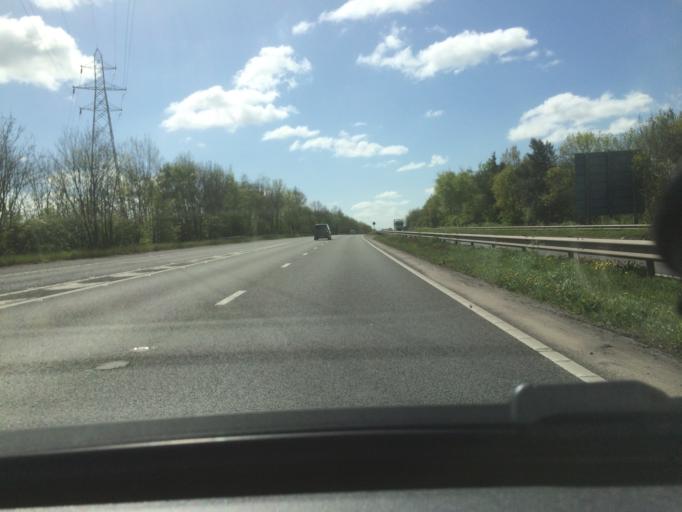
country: GB
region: Wales
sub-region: Wrexham
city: Rhosllanerchrugog
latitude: 53.0241
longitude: -3.0285
